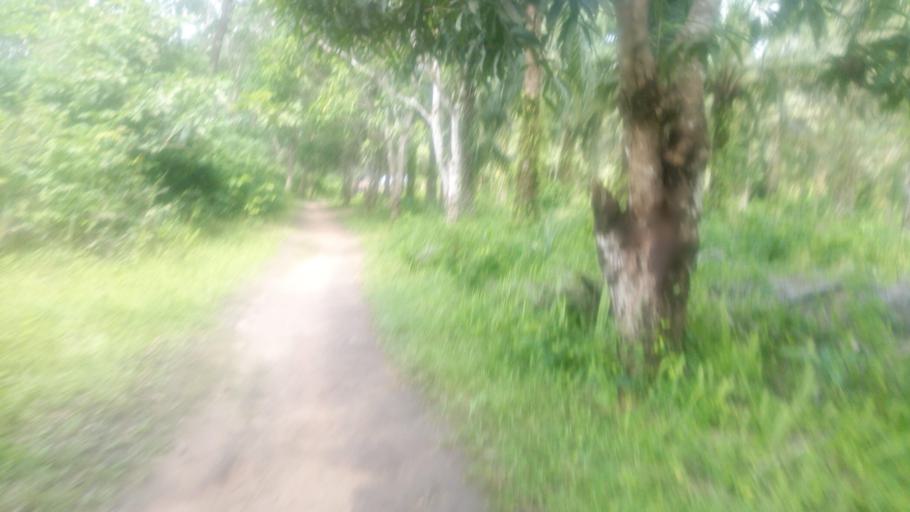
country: SL
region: Northern Province
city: Magburaka
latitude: 8.6668
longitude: -12.0607
